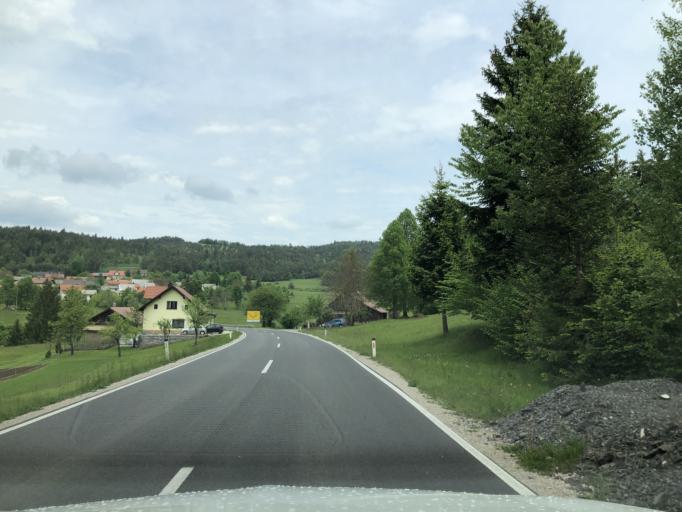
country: SI
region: Bloke
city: Nova Vas
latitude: 45.7560
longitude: 14.4694
